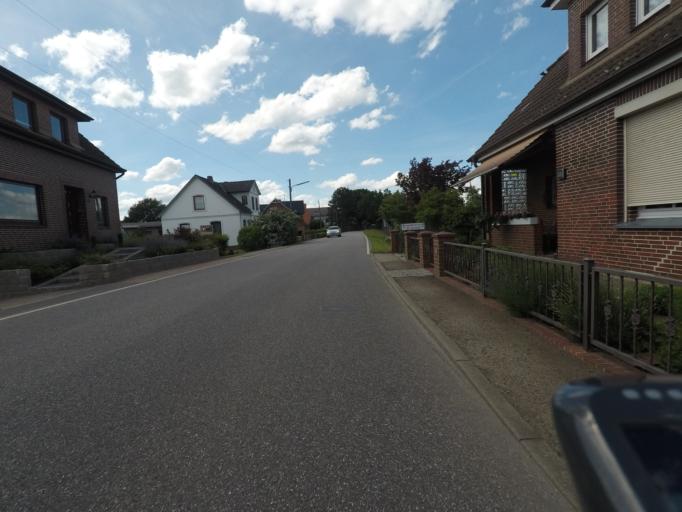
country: DE
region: Lower Saxony
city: Drage
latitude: 53.4299
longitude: 10.2436
